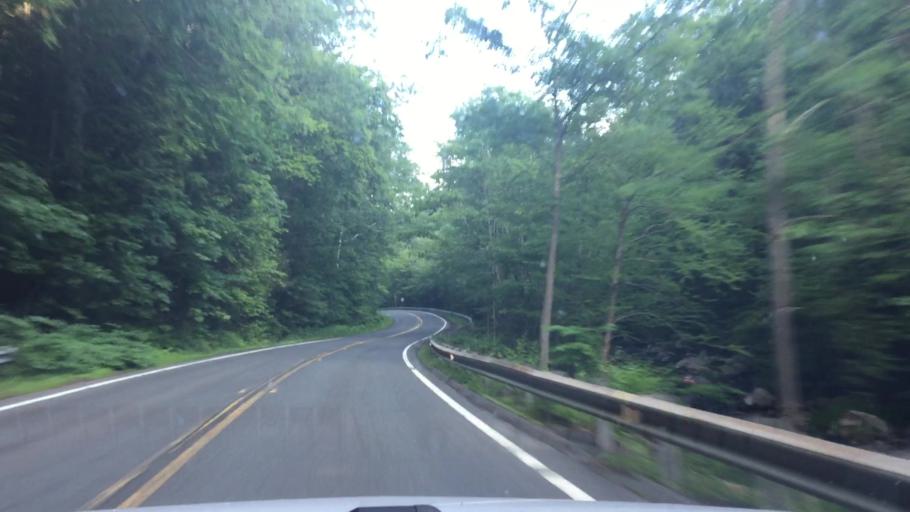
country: US
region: Massachusetts
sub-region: Hampshire County
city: Chesterfield
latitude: 42.3288
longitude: -72.8753
